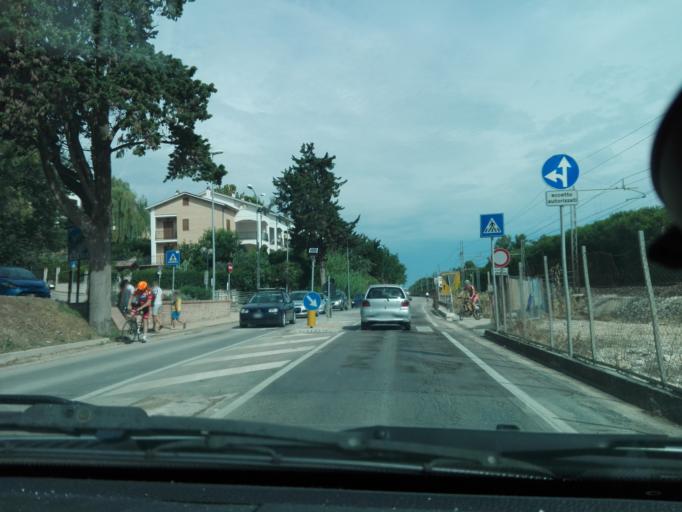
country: IT
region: Abruzzo
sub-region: Provincia di Teramo
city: Pineto
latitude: 42.5895
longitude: 14.0842
